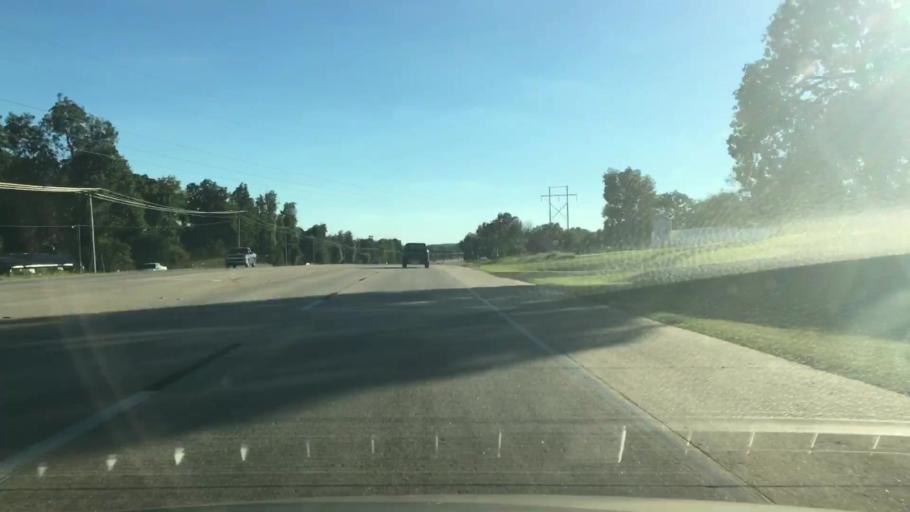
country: US
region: Oklahoma
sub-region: Cherokee County
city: Park Hill
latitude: 35.8310
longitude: -95.0434
